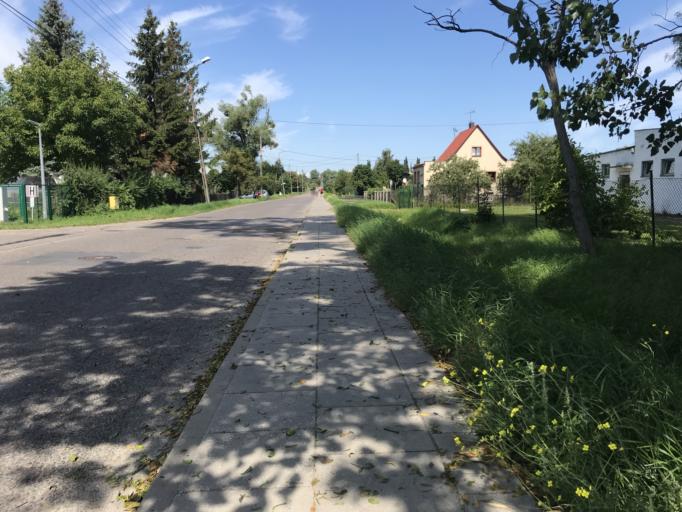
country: PL
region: Pomeranian Voivodeship
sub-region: Gdansk
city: Gdansk
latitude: 54.3389
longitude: 18.6730
